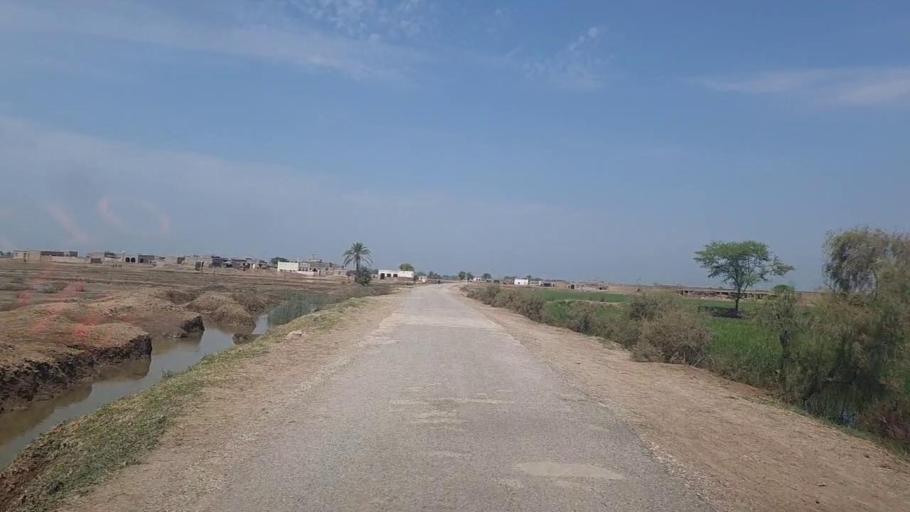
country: PK
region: Sindh
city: Thul
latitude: 28.2907
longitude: 68.6833
